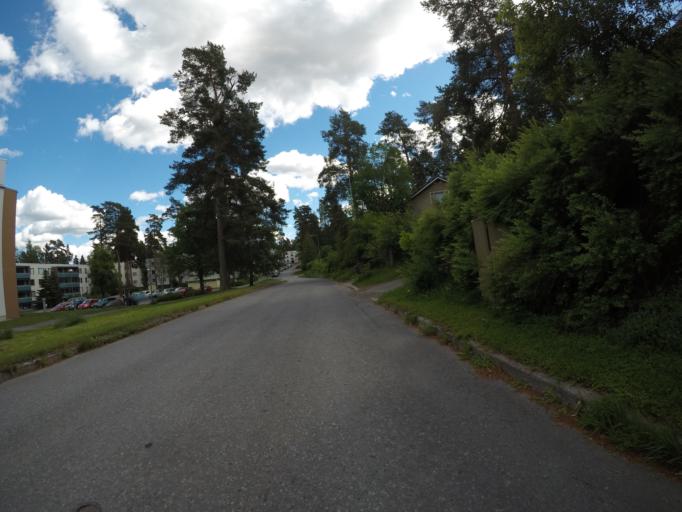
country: FI
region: Haeme
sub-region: Haemeenlinna
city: Haemeenlinna
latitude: 61.0156
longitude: 24.4340
